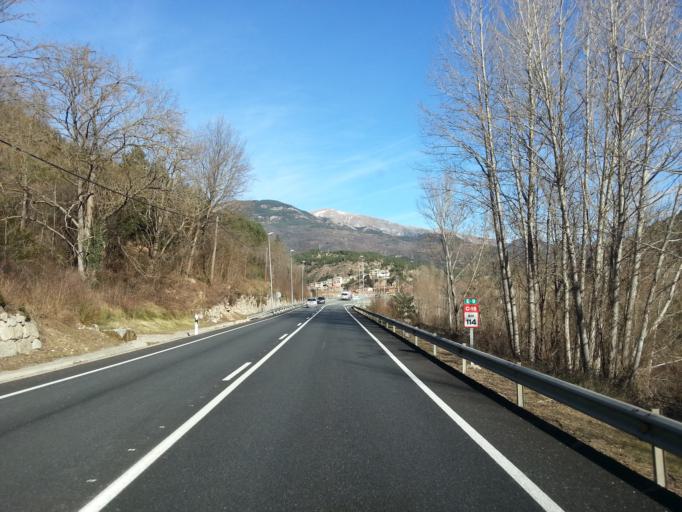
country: ES
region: Catalonia
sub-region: Provincia de Barcelona
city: Guardiola de Bergueda
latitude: 42.2261
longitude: 1.8744
